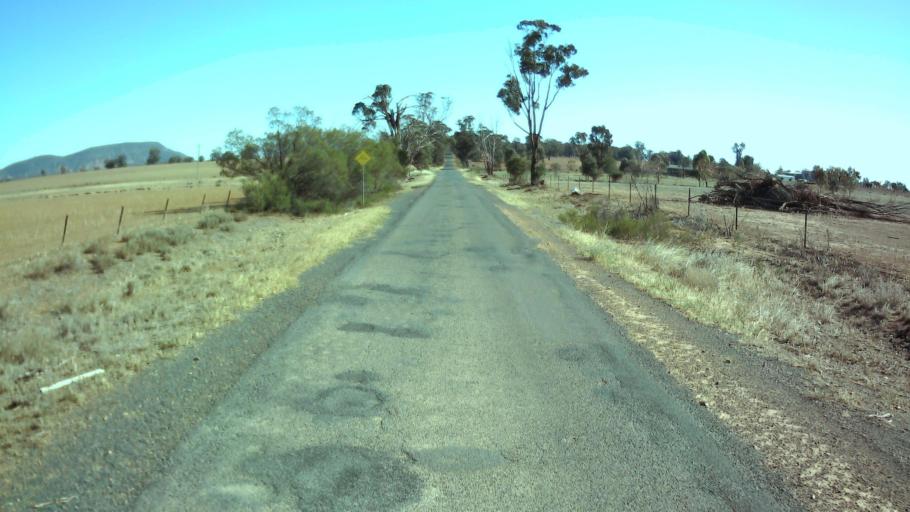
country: AU
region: New South Wales
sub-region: Weddin
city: Grenfell
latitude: -33.7946
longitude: 147.9569
